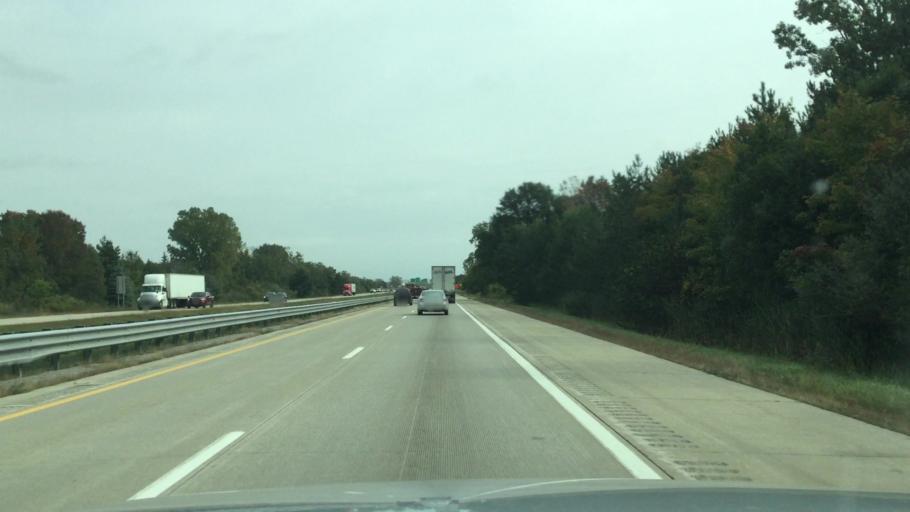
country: US
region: Michigan
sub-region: Genesee County
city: Swartz Creek
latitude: 42.9678
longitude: -83.7797
